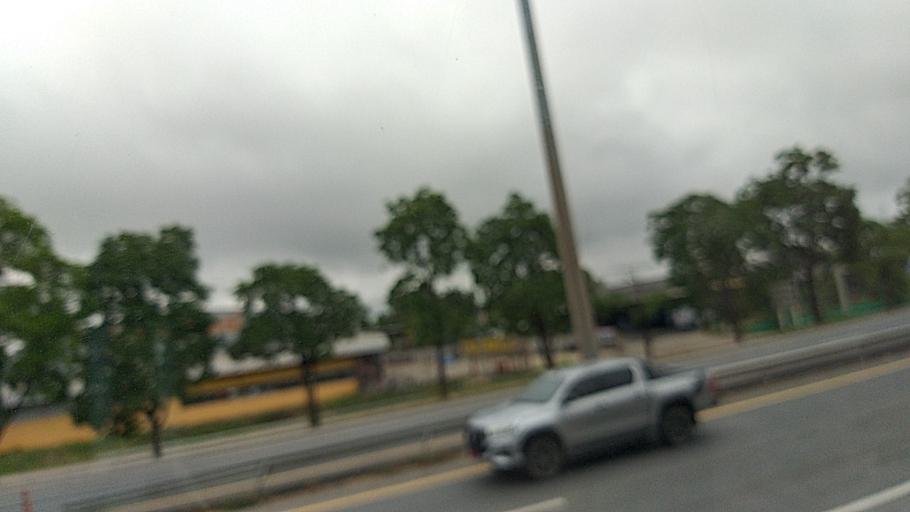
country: TH
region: Nakhon Ratchasima
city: Nakhon Ratchasima
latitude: 15.0569
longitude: 102.1620
